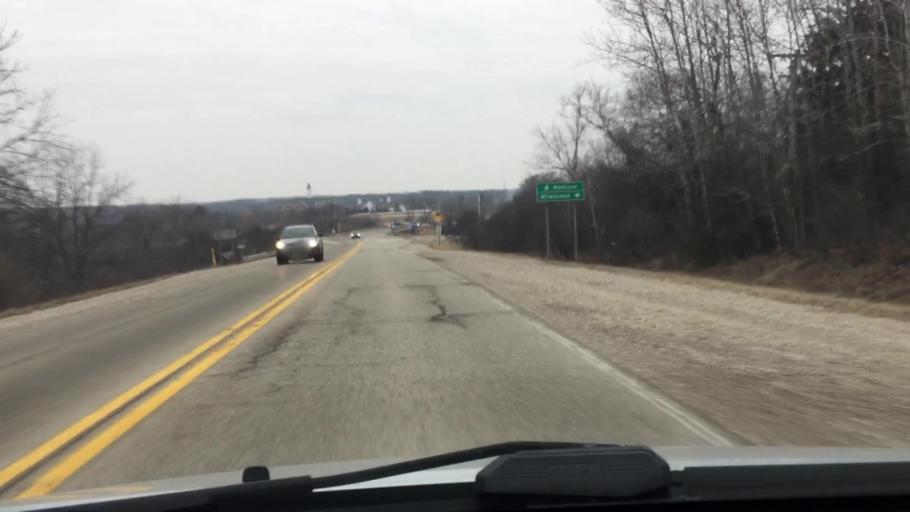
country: US
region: Wisconsin
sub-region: Waukesha County
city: Delafield
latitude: 43.0513
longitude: -88.4044
